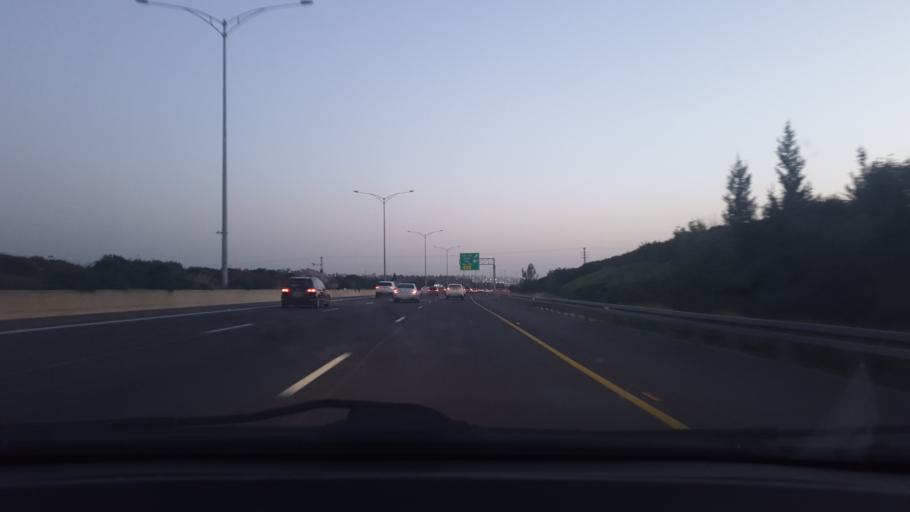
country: IL
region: Central District
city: Jaljulya
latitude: 32.1542
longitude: 34.9625
